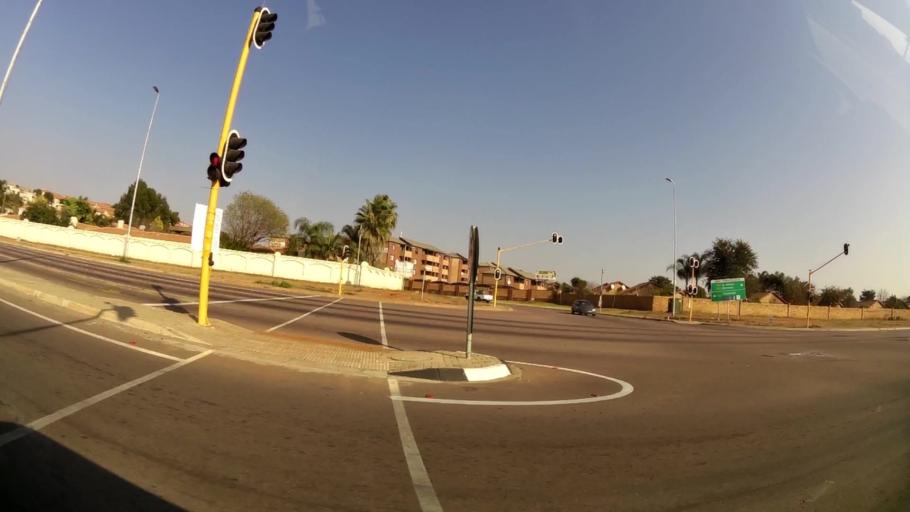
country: ZA
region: Gauteng
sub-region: City of Tshwane Metropolitan Municipality
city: Pretoria
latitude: -25.7443
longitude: 28.3279
